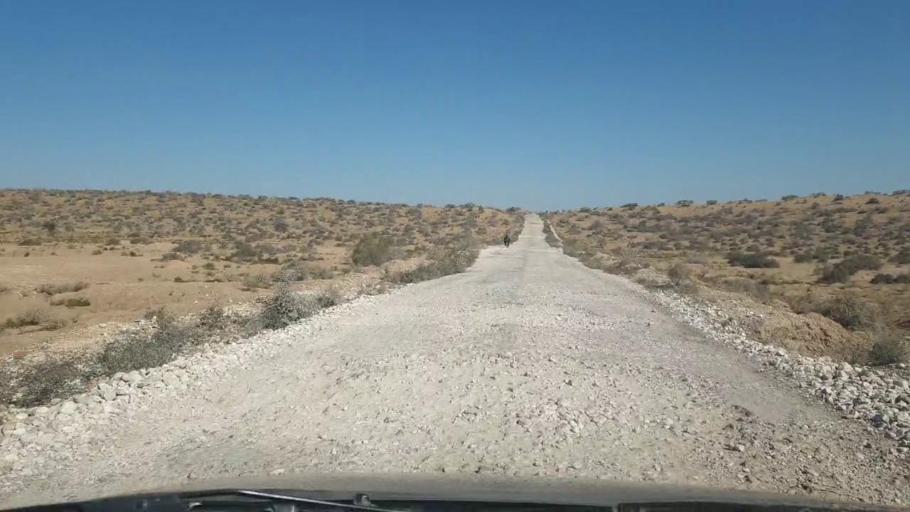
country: PK
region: Sindh
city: Bozdar
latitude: 27.0005
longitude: 68.8346
